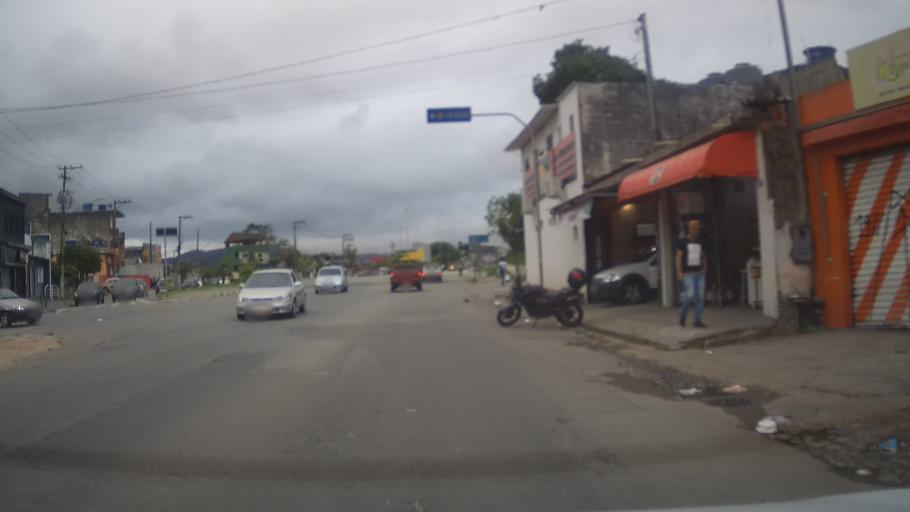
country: BR
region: Sao Paulo
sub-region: Guarulhos
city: Guarulhos
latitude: -23.4111
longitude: -46.4525
